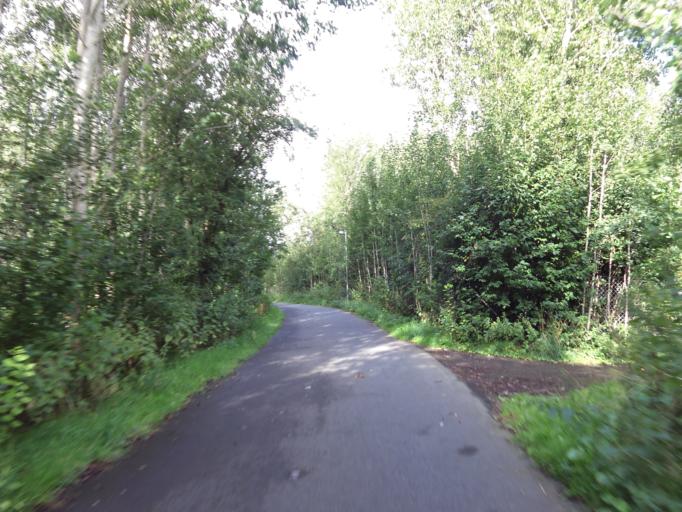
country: DK
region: South Denmark
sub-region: Esbjerg Kommune
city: Ribe
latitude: 55.3339
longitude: 8.7776
